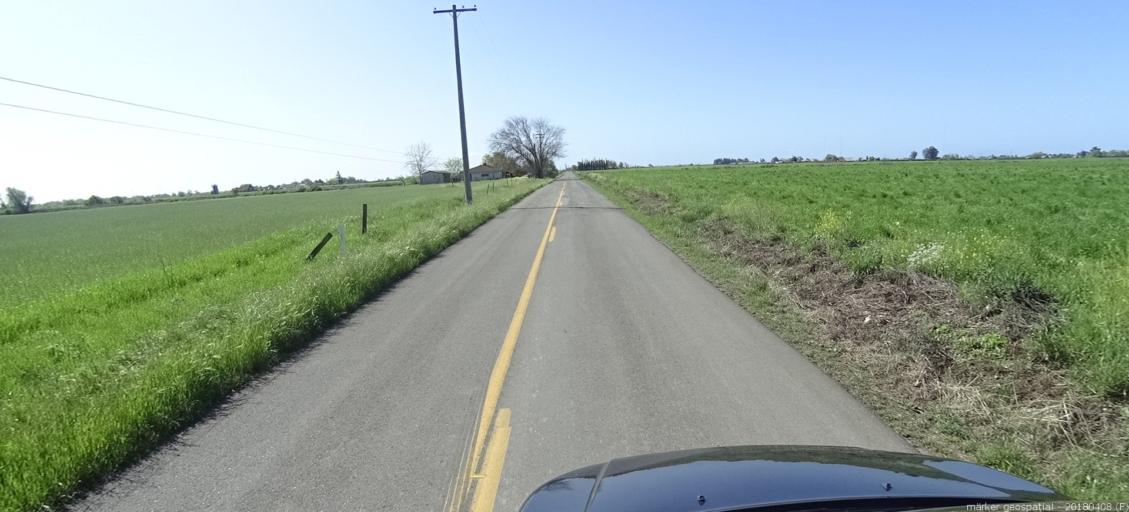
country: US
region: California
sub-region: Sacramento County
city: Laguna
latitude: 38.3501
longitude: -121.4359
